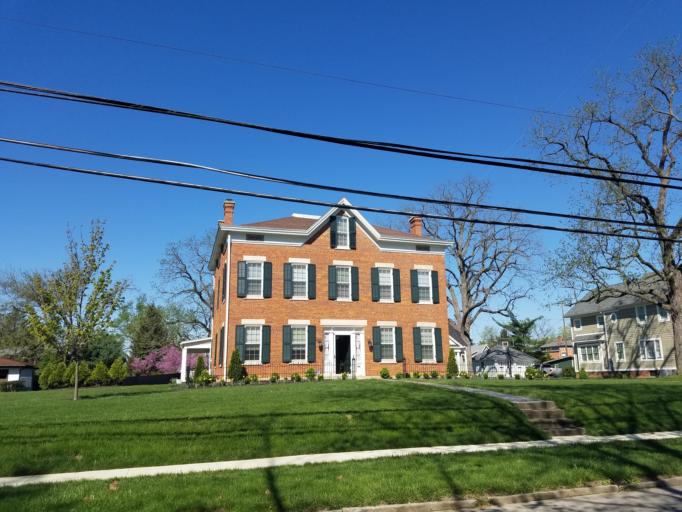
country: US
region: Ohio
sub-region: Seneca County
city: Tiffin
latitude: 41.1044
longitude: -83.1750
